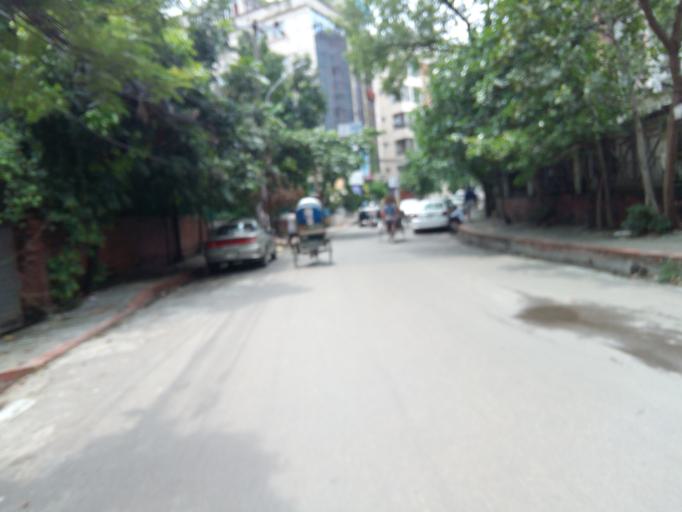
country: BD
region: Dhaka
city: Azimpur
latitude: 23.7453
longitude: 90.3797
